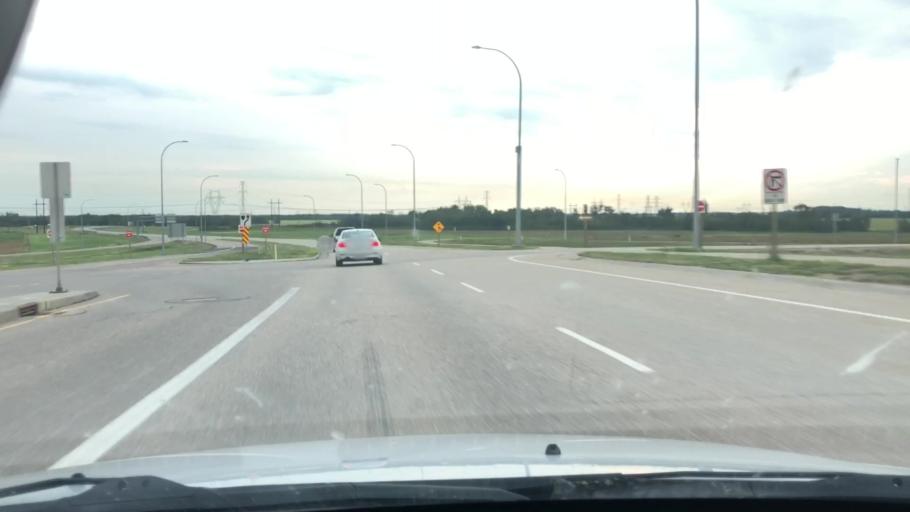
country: CA
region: Alberta
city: Devon
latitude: 53.4662
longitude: -113.6324
